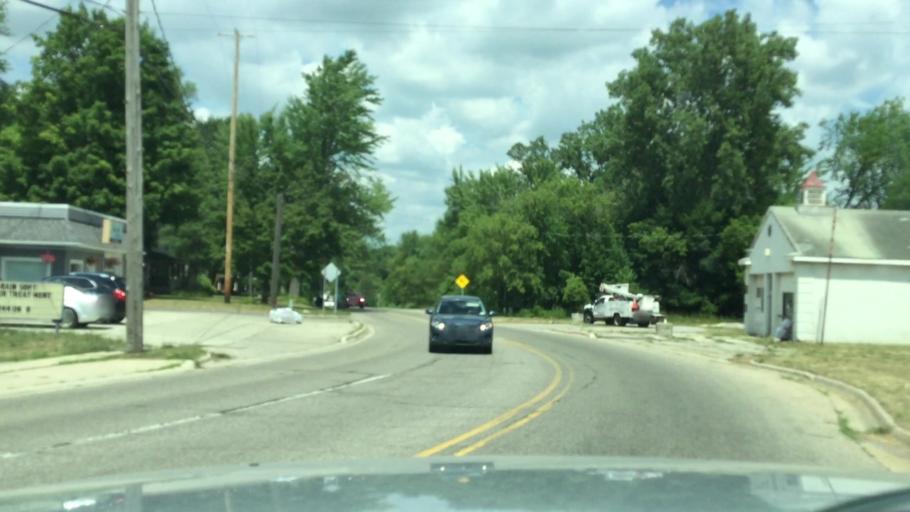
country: US
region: Michigan
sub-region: Genesee County
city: Flushing
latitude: 43.0632
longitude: -83.8625
